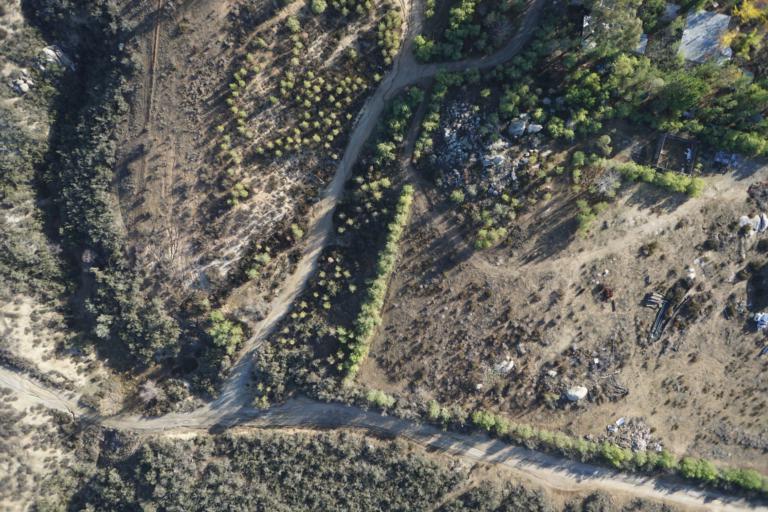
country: US
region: California
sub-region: Riverside County
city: East Hemet
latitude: 33.6137
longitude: -116.9107
